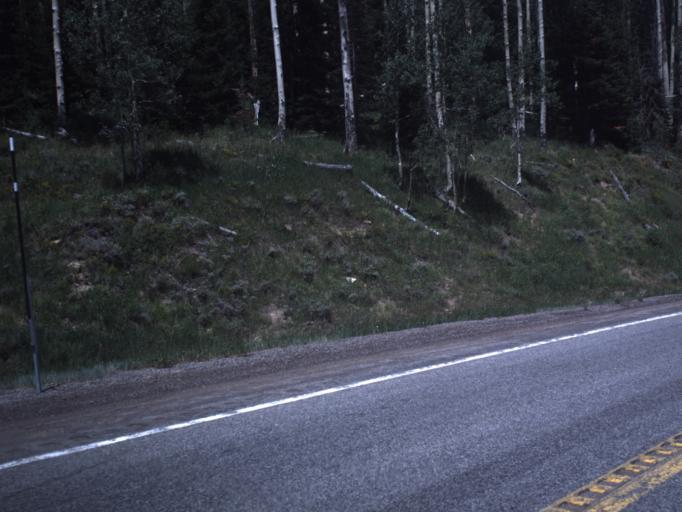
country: US
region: Utah
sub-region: Sanpete County
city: Fairview
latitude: 39.5948
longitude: -111.2277
